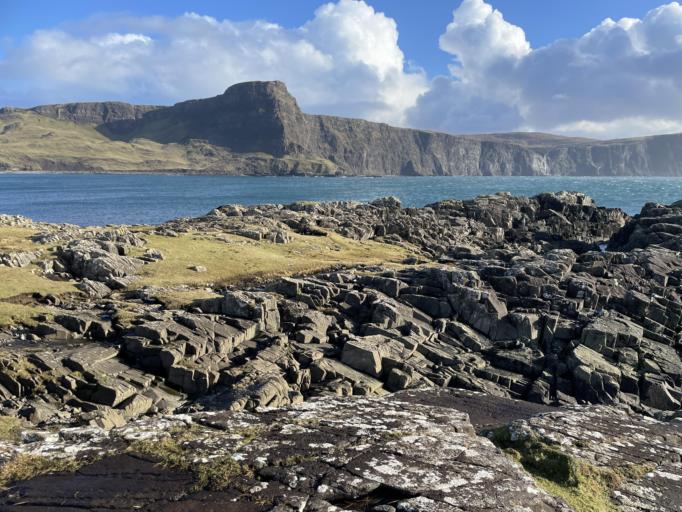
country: GB
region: Scotland
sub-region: Eilean Siar
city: Harris
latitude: 57.4210
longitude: -6.7849
